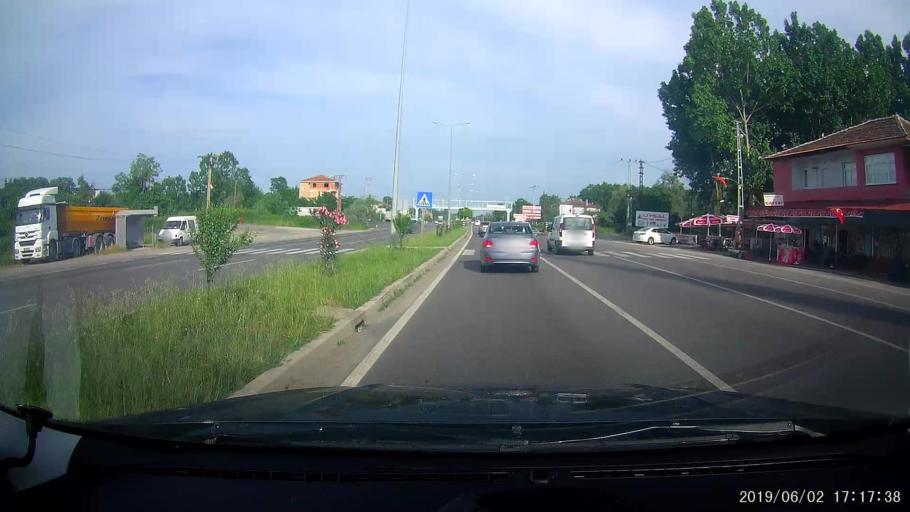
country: TR
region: Samsun
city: Dikbiyik
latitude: 41.2273
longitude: 36.5853
